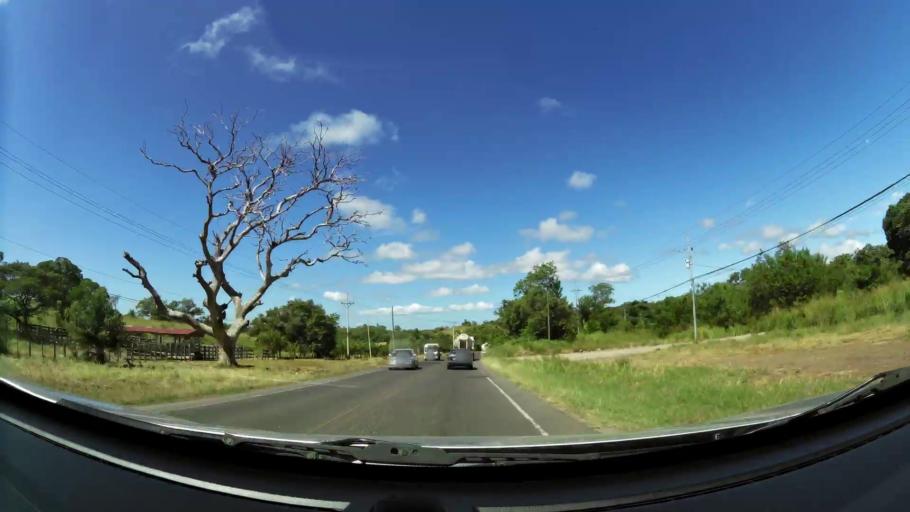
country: CR
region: Guanacaste
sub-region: Canton de Canas
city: Canas
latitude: 10.4041
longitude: -85.0853
